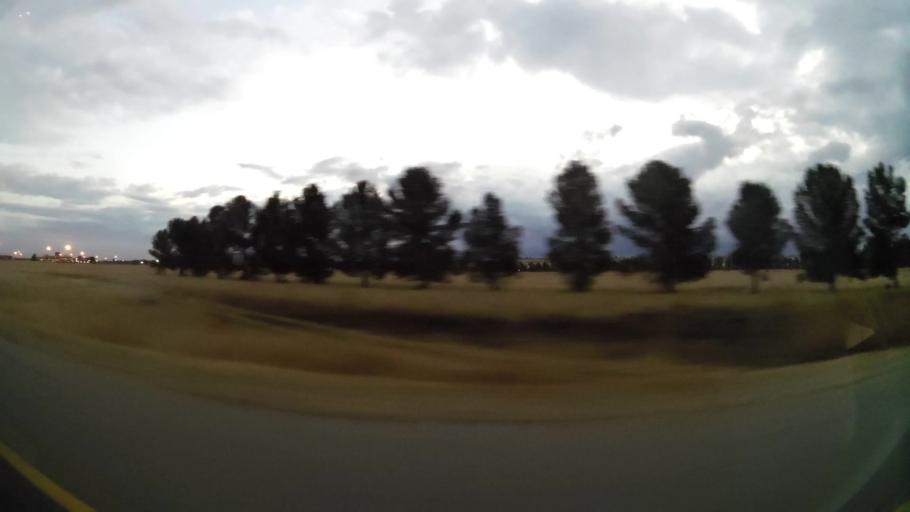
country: ZA
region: Orange Free State
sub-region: Lejweleputswa District Municipality
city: Welkom
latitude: -27.9395
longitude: 26.7886
